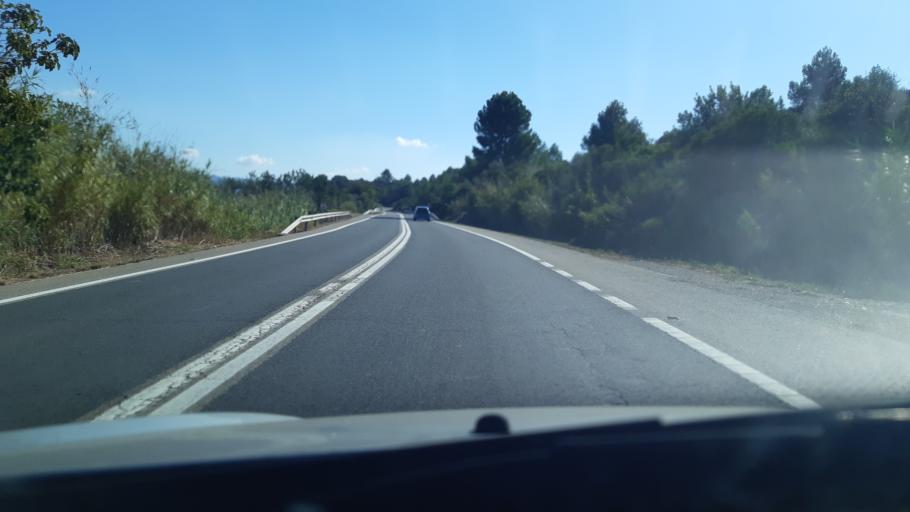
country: ES
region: Catalonia
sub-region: Provincia de Tarragona
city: Tivenys
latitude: 40.9014
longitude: 0.4830
